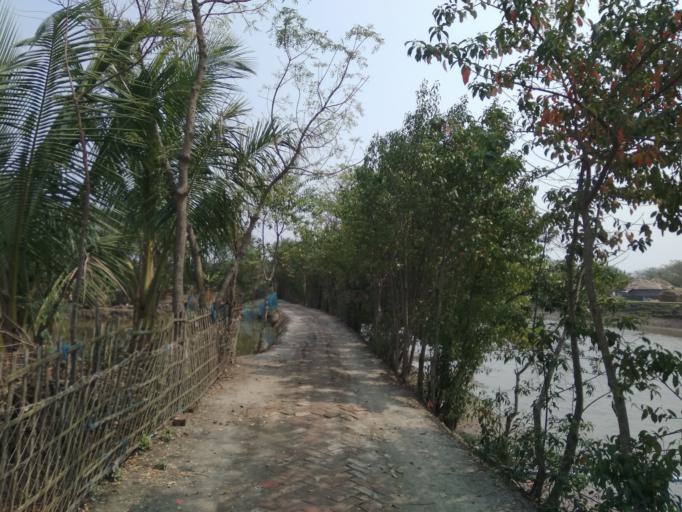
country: IN
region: West Bengal
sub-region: North 24 Parganas
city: Taki
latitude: 22.2569
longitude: 89.2567
